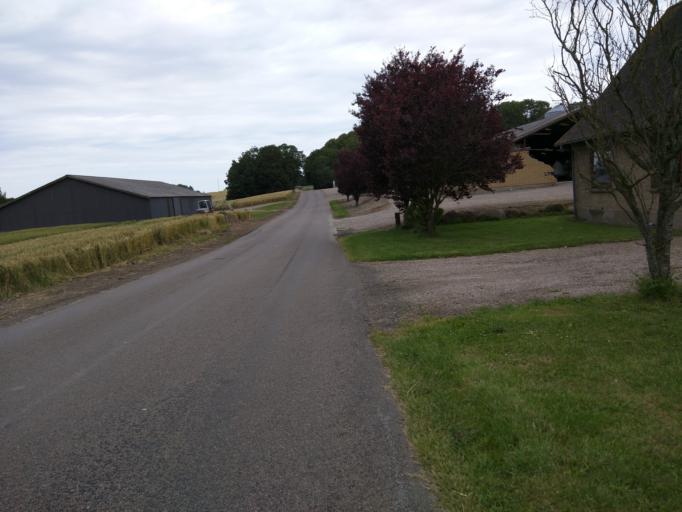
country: DK
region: Zealand
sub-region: Kalundborg Kommune
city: Svebolle
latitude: 55.6963
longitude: 11.3065
